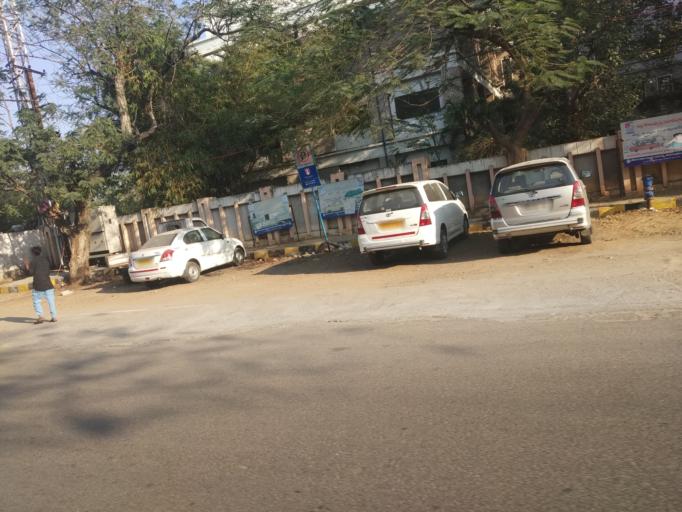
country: IN
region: Telangana
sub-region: Rangareddi
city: Kukatpalli
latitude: 17.4567
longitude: 78.4416
